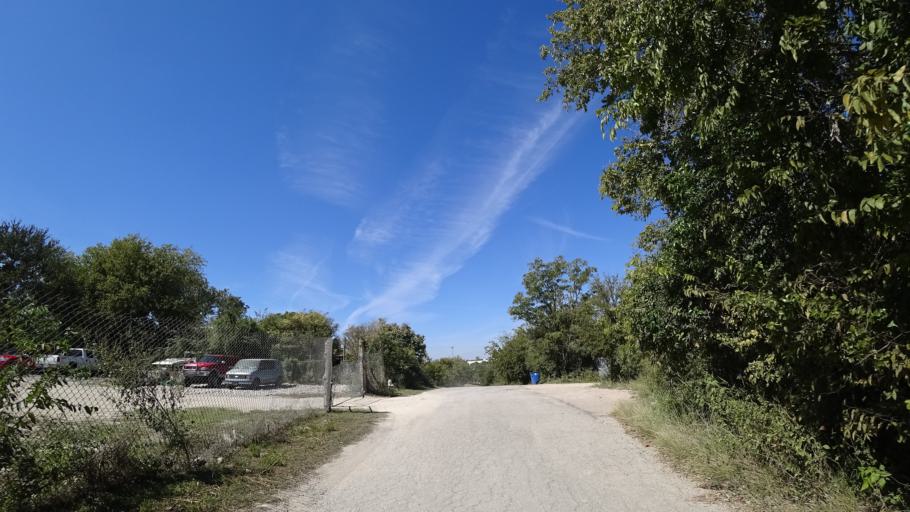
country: US
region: Texas
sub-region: Travis County
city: Austin
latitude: 30.2121
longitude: -97.6880
